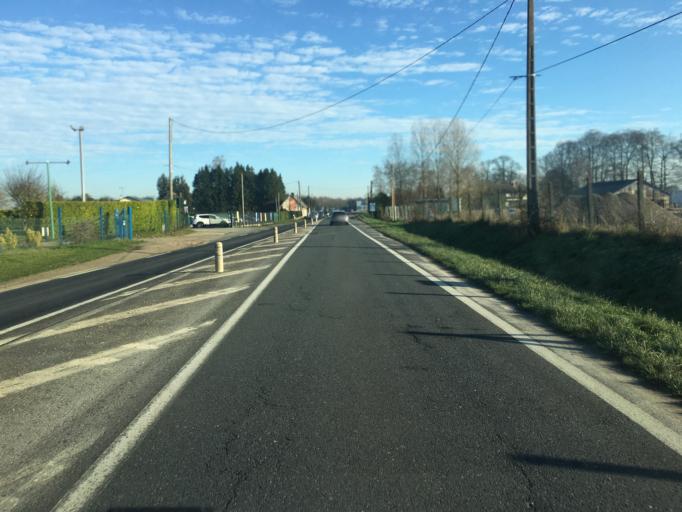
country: FR
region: Haute-Normandie
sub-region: Departement de la Seine-Maritime
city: Sainte-Marie-des-Champs
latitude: 49.6268
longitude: 0.7952
